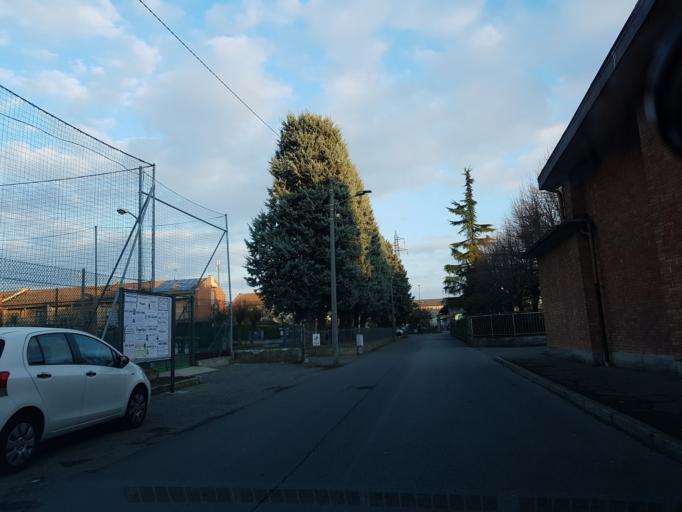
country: IT
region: Piedmont
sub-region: Provincia di Alessandria
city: Novi Ligure
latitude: 44.7705
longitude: 8.7927
